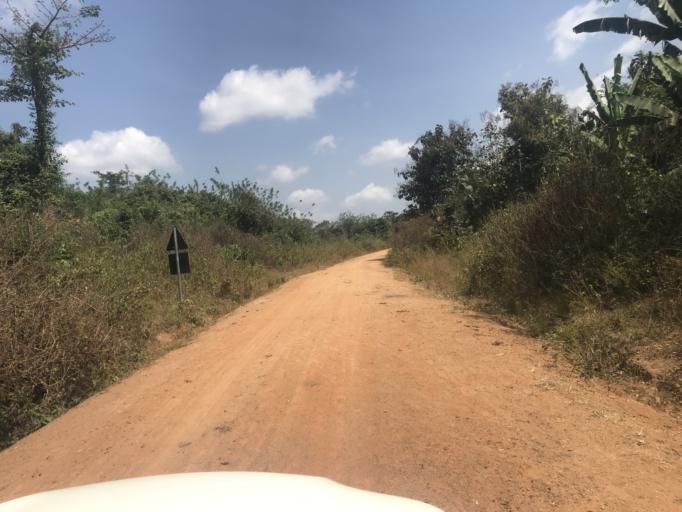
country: NG
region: Osun
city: Otan Ayegbaju
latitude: 7.8929
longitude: 4.8526
